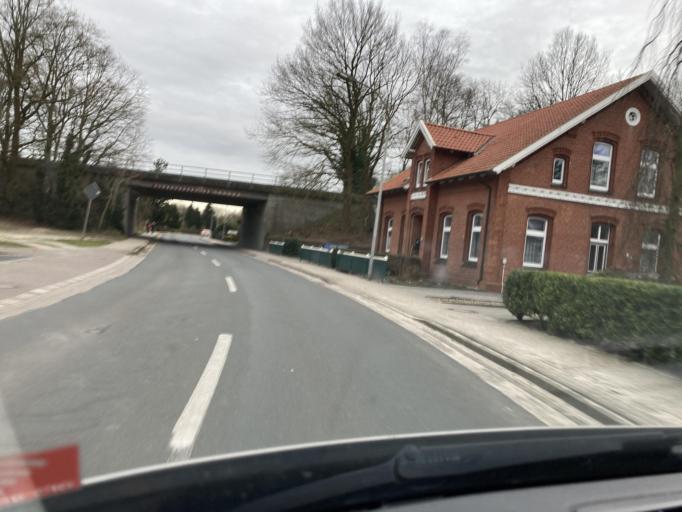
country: DE
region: Lower Saxony
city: Leer
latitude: 53.1616
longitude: 7.4603
